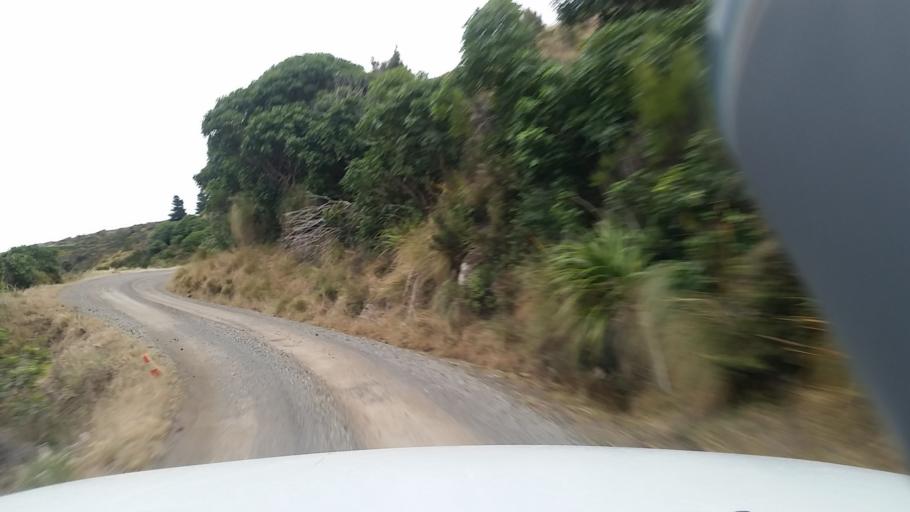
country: NZ
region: Canterbury
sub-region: Christchurch City
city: Christchurch
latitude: -43.8069
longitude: 172.8503
